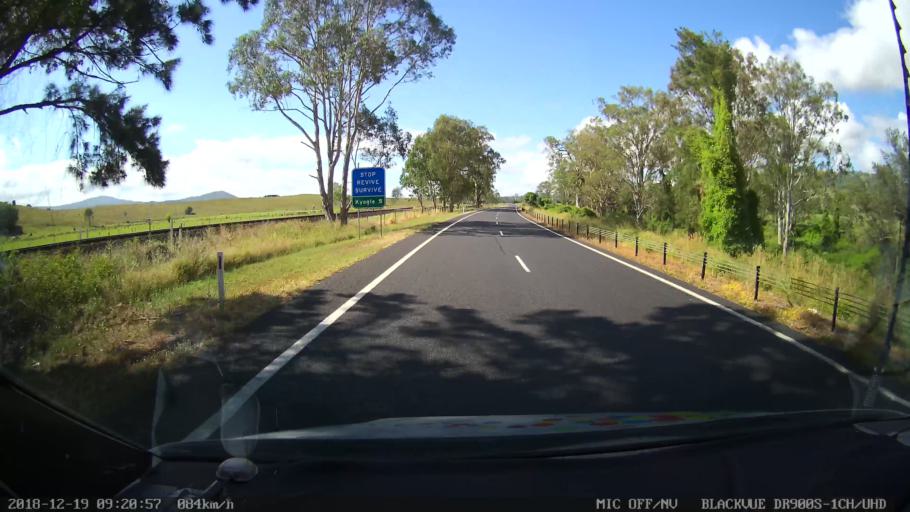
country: AU
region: New South Wales
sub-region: Kyogle
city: Kyogle
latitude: -28.5775
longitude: 152.9826
